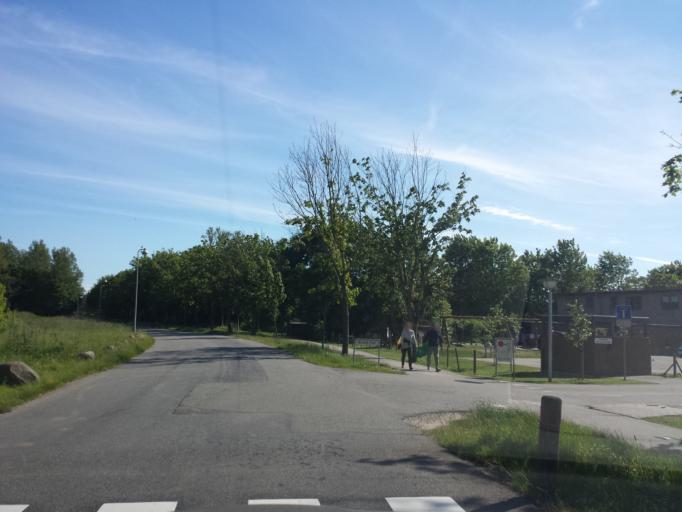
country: DK
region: Capital Region
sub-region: Ballerup Kommune
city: Ballerup
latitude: 55.7189
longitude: 12.3752
